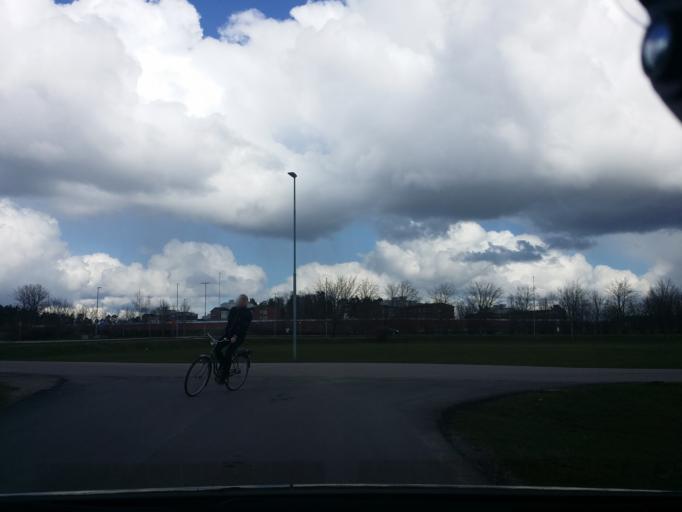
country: SE
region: Vaestmanland
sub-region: Sala Kommun
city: Sala
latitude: 59.9227
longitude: 16.5783
